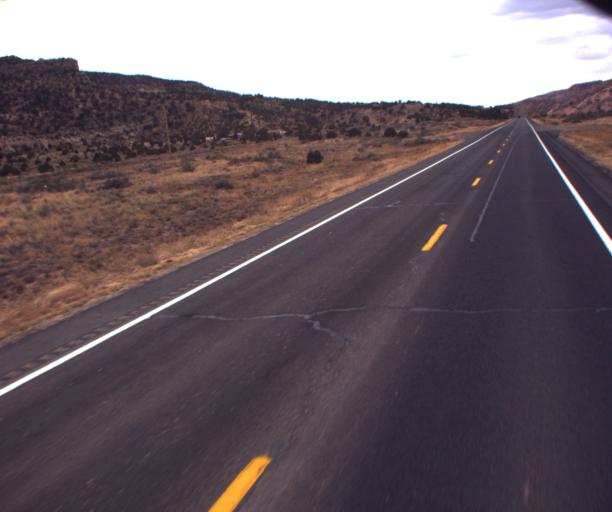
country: US
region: Arizona
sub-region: Navajo County
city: Kayenta
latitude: 36.6698
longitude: -110.4051
